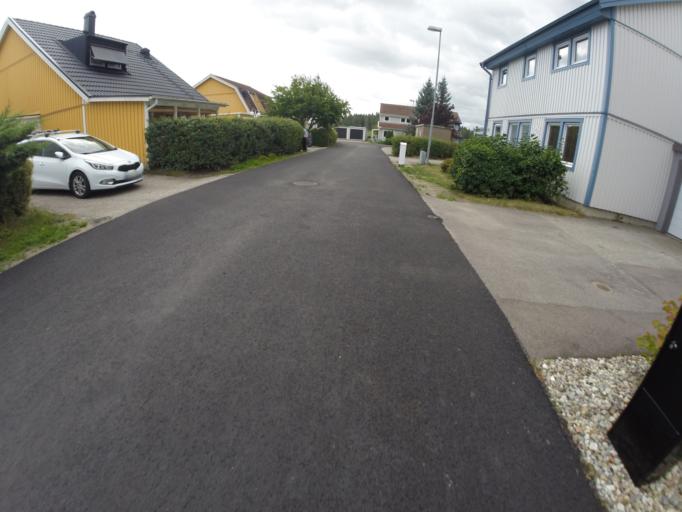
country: SE
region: Soedermanland
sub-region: Eskilstuna Kommun
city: Torshalla
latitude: 59.4083
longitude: 16.4932
